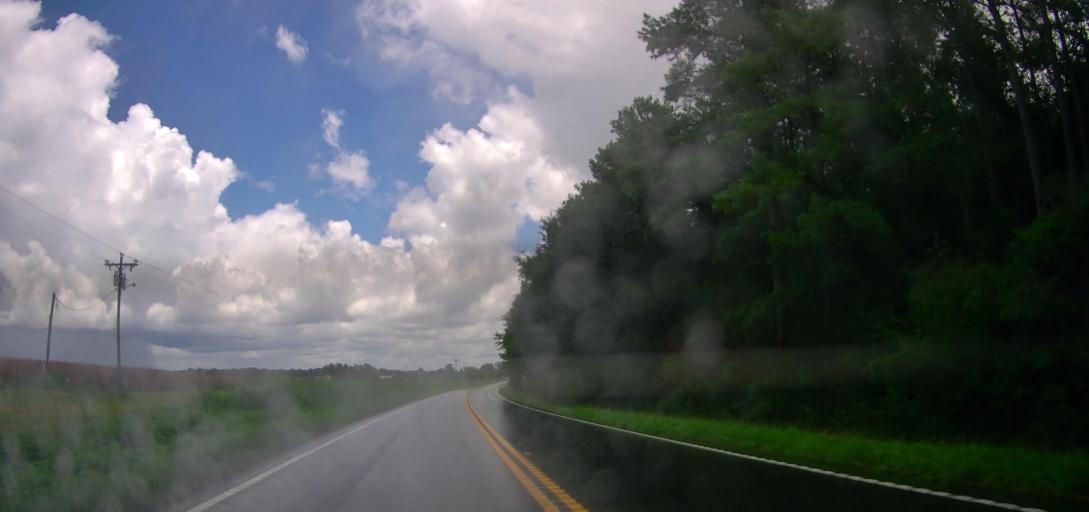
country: US
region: Georgia
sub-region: Pulaski County
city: Hawkinsville
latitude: 32.1794
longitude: -83.5343
